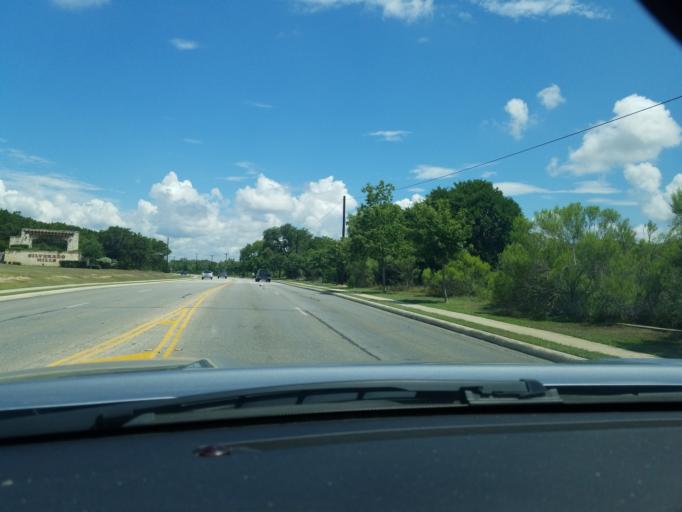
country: US
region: Texas
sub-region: Bexar County
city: Timberwood Park
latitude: 29.6921
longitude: -98.4789
